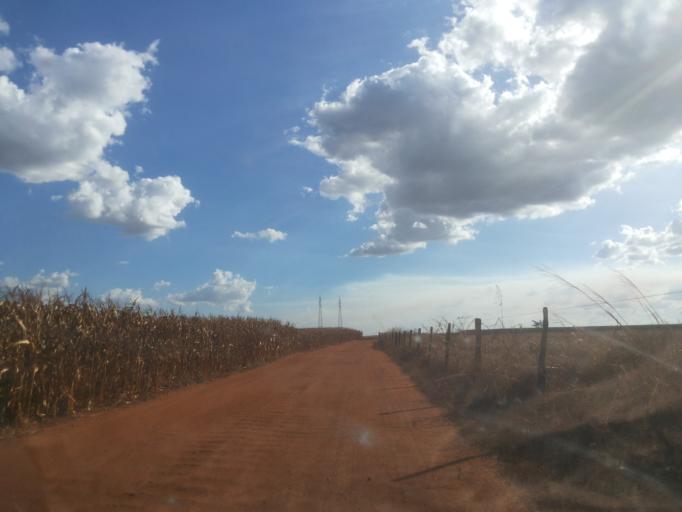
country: BR
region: Minas Gerais
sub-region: Capinopolis
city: Capinopolis
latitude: -18.5826
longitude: -49.5030
